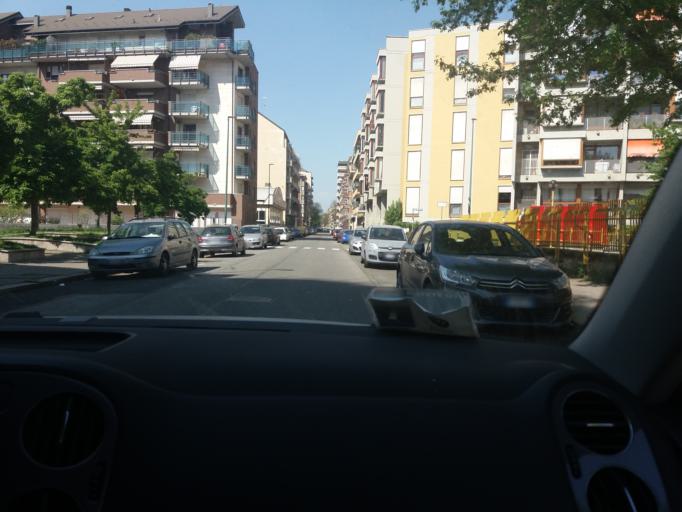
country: IT
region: Piedmont
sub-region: Provincia di Torino
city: Lesna
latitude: 45.0690
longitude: 7.6305
